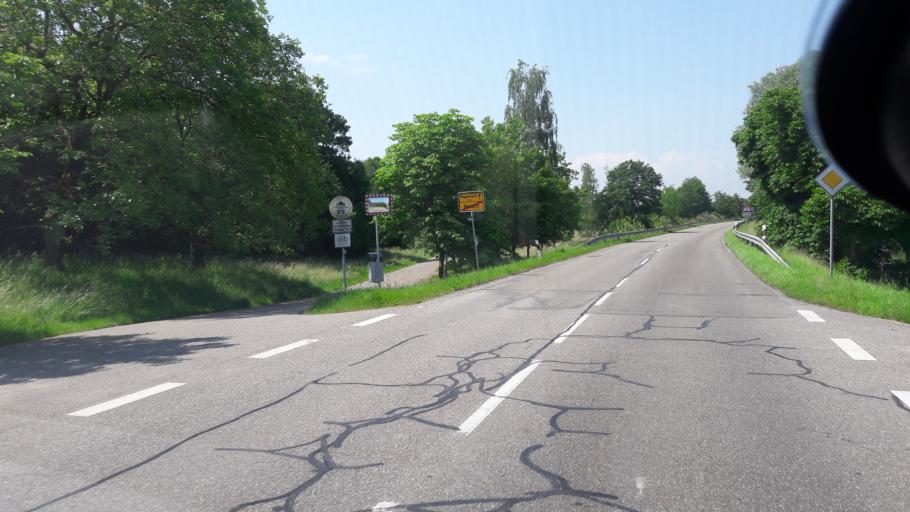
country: DE
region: Baden-Wuerttemberg
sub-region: Karlsruhe Region
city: Malsch
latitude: 48.8737
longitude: 8.3223
